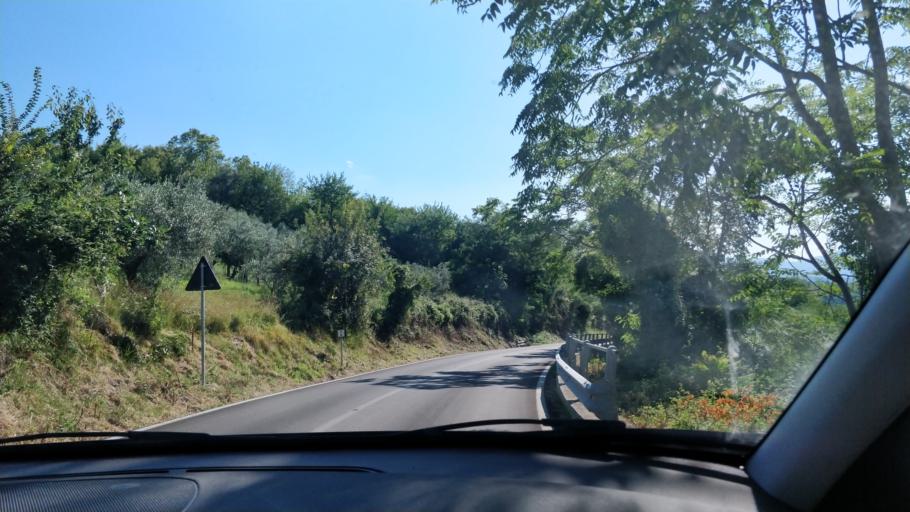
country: IT
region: Abruzzo
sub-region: Provincia di Pescara
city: Serramonacesca
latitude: 42.2552
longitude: 14.0888
